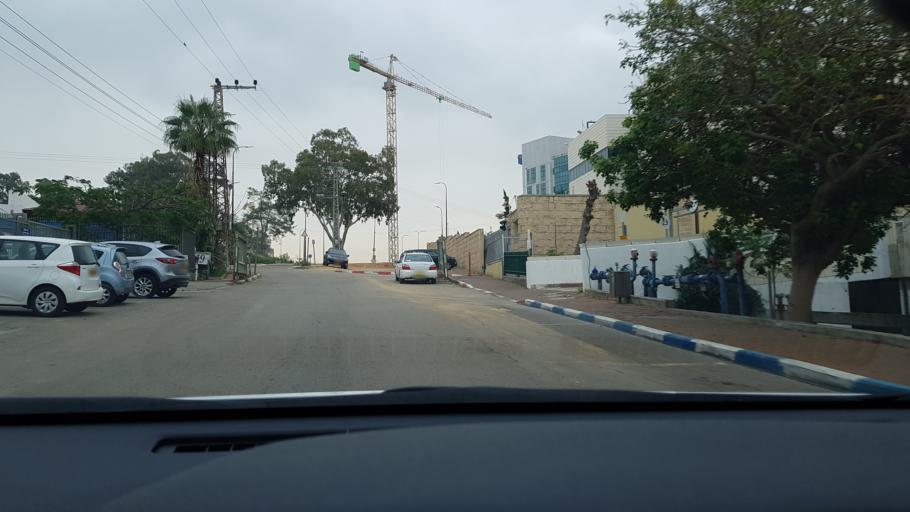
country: IL
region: Central District
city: Ness Ziona
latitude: 31.9159
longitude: 34.8067
